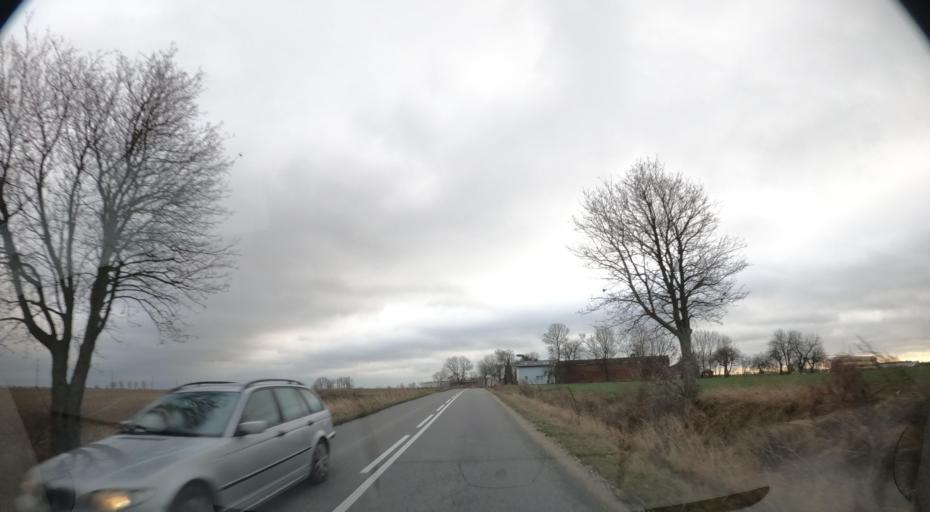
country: PL
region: Kujawsko-Pomorskie
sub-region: Powiat nakielski
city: Sadki
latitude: 53.1702
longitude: 17.4333
